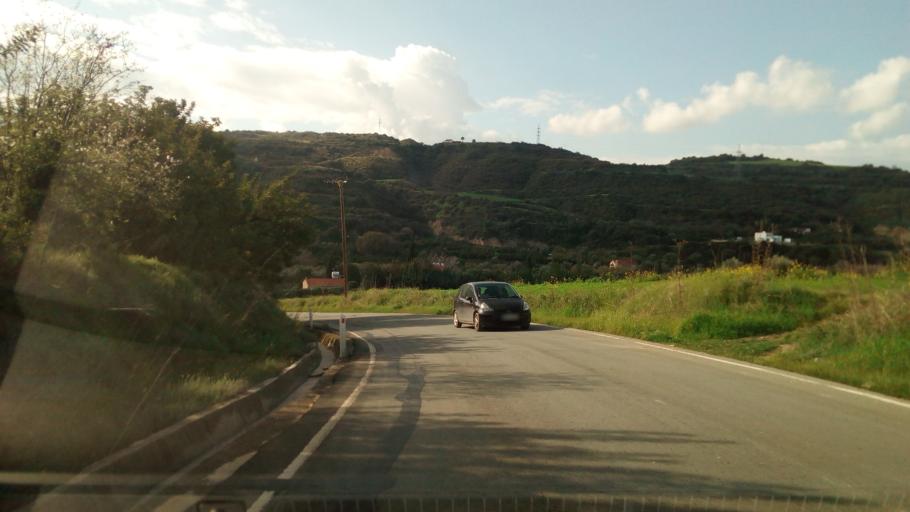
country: CY
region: Pafos
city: Polis
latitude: 34.9804
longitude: 32.4637
